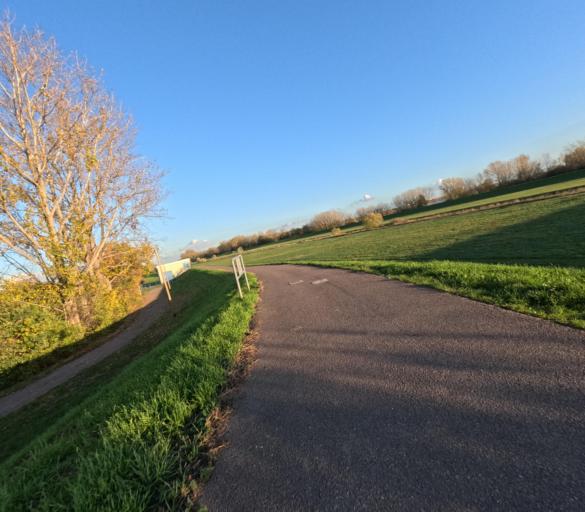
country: DE
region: Saxony-Anhalt
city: Rassnitz
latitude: 51.3897
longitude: 12.0944
